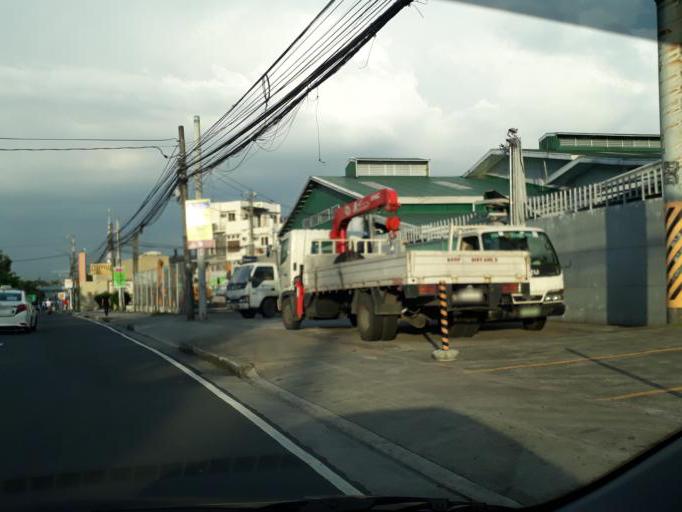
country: PH
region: Calabarzon
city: Bagong Pagasa
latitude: 14.6653
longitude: 121.0297
